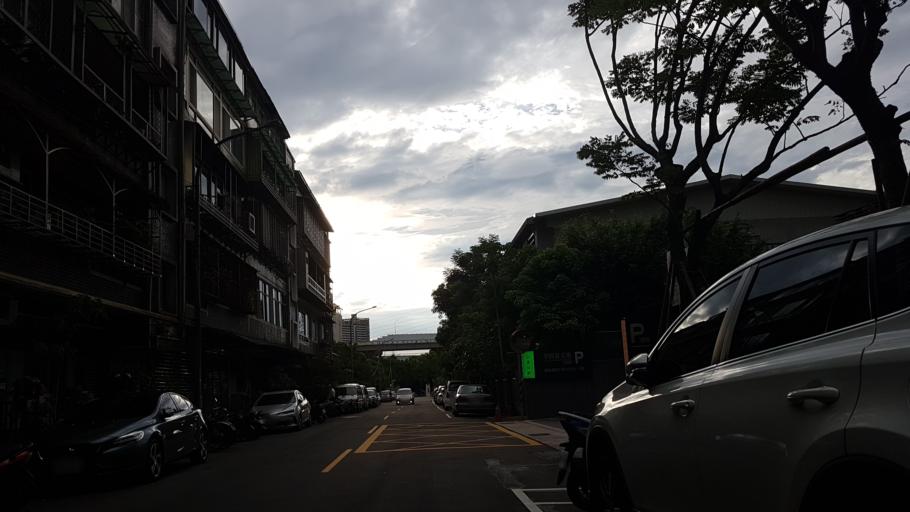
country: TW
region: Taipei
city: Taipei
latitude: 24.9962
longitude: 121.5376
